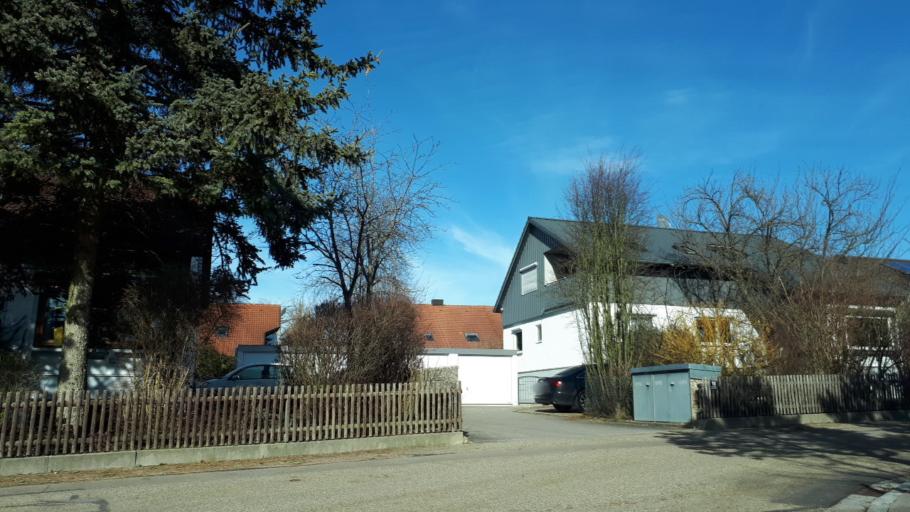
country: DE
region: Bavaria
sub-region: Upper Palatinate
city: Pentling
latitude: 48.9869
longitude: 12.0566
